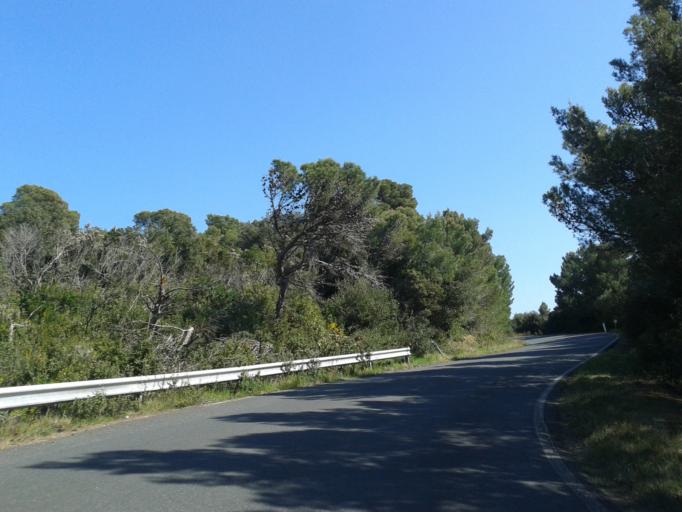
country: IT
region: Tuscany
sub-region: Provincia di Livorno
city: Quercianella
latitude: 43.4485
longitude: 10.3921
